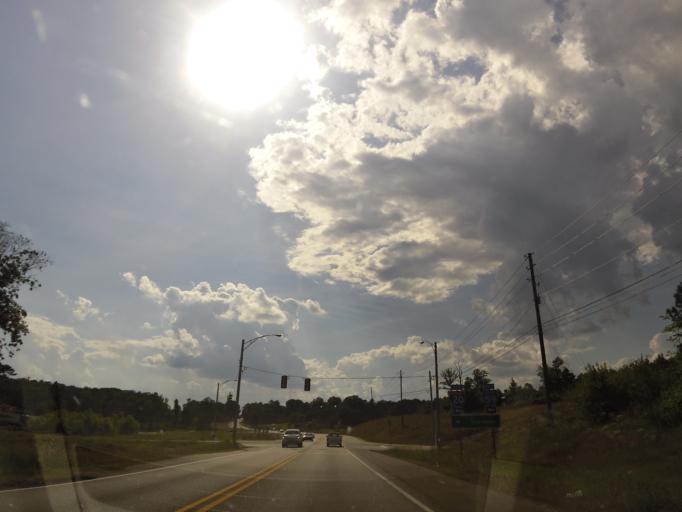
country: US
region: Alabama
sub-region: Tuscaloosa County
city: Lake View
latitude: 33.2797
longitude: -87.0961
